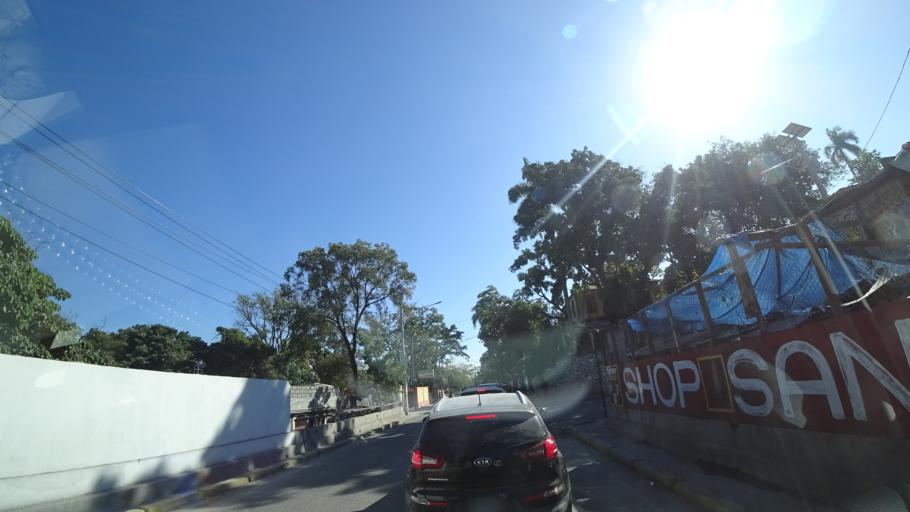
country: HT
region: Ouest
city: Petionville
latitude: 18.5117
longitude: -72.2844
